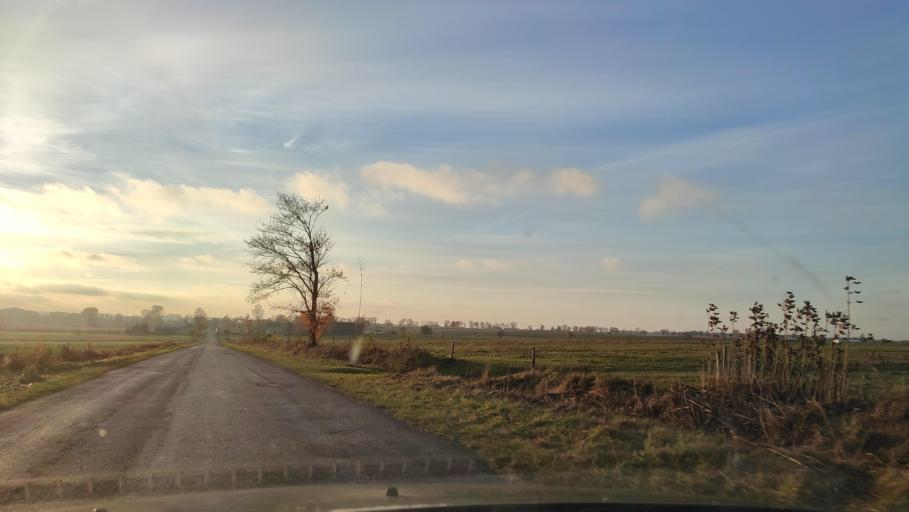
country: PL
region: Masovian Voivodeship
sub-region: Powiat mlawski
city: Wieczfnia Koscielna
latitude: 53.2384
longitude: 20.5681
